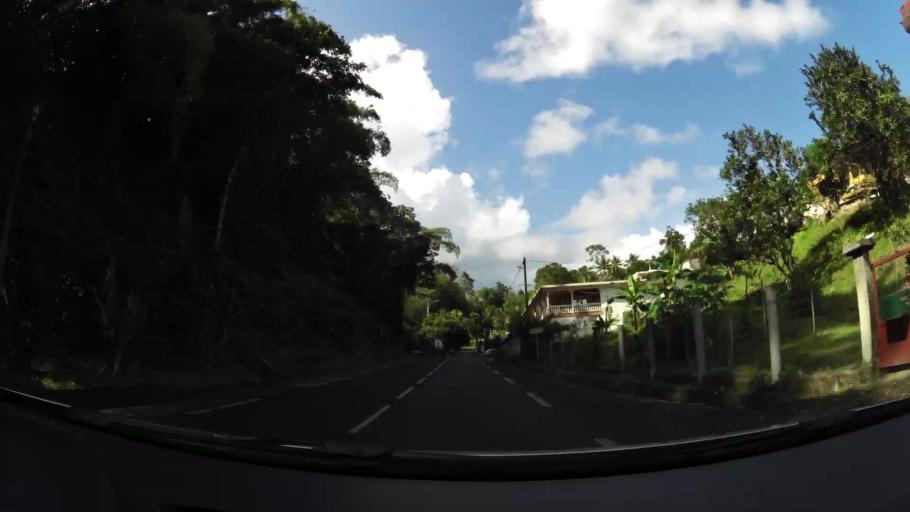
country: MQ
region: Martinique
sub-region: Martinique
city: Basse-Pointe
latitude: 14.8309
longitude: -61.1032
